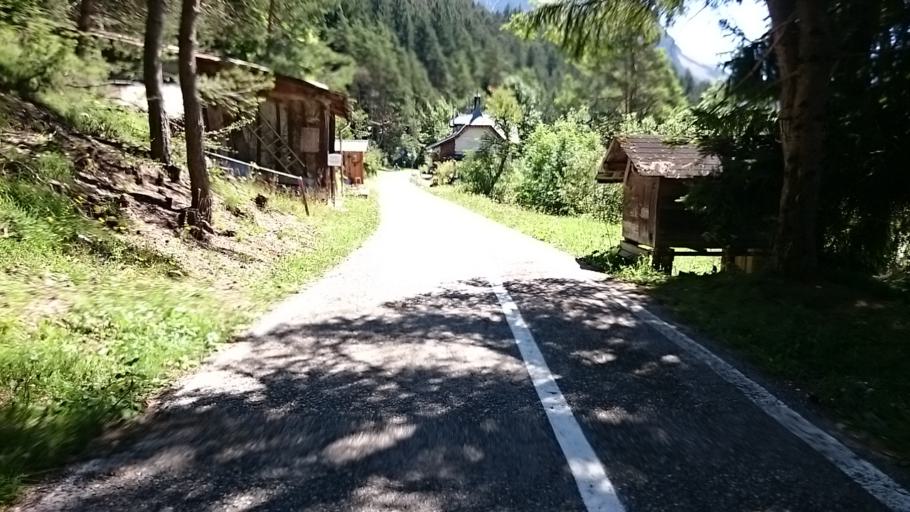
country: IT
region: Veneto
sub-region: Provincia di Belluno
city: San Vito
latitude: 46.4751
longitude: 12.2028
